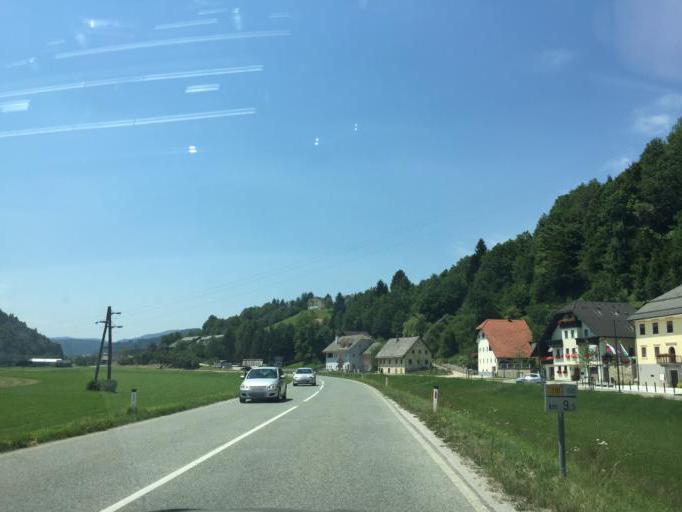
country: SI
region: Gorenja Vas-Poljane
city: Gorenja Vas
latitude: 46.1201
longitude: 14.1842
